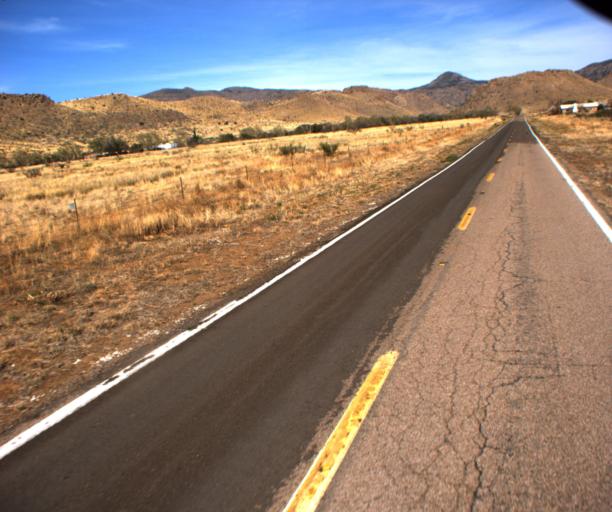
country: US
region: Arizona
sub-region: Cochise County
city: Willcox
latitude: 32.0067
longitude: -109.4103
